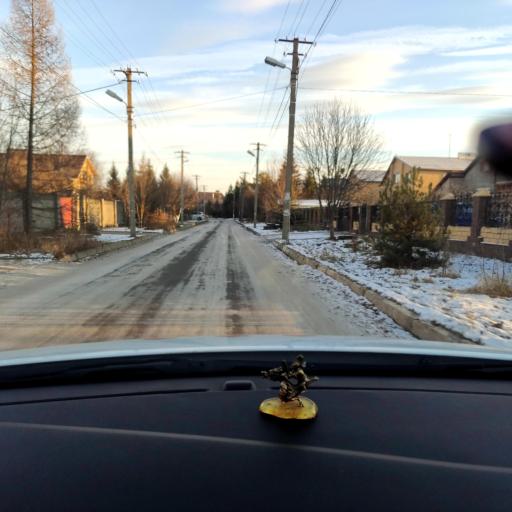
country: RU
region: Tatarstan
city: Stolbishchi
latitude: 55.6072
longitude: 49.1388
